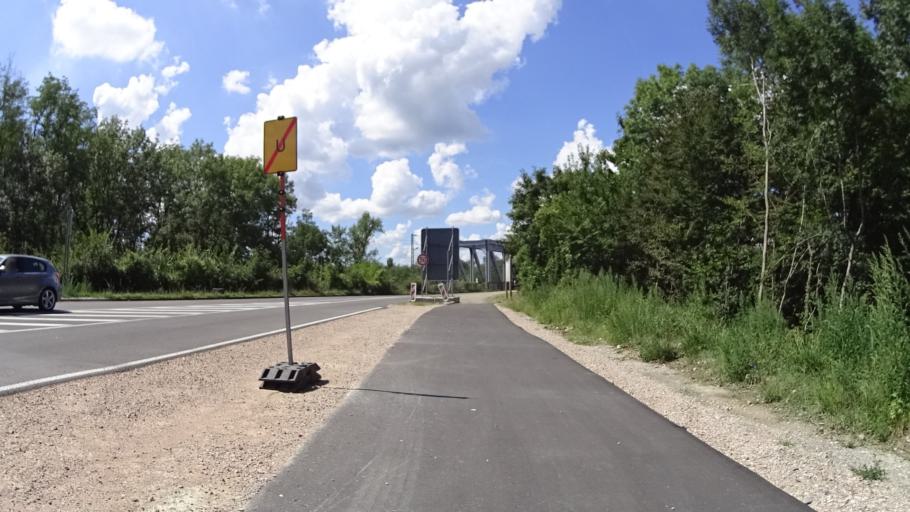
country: FR
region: Alsace
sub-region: Departement du Haut-Rhin
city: Chalampe
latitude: 47.8142
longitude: 7.5488
